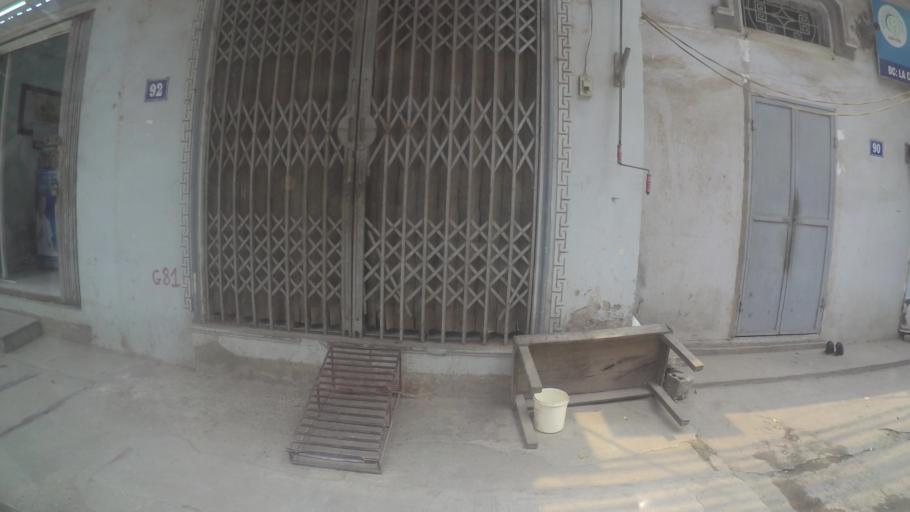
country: VN
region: Ha Noi
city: Ha Dong
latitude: 20.9806
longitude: 105.7487
